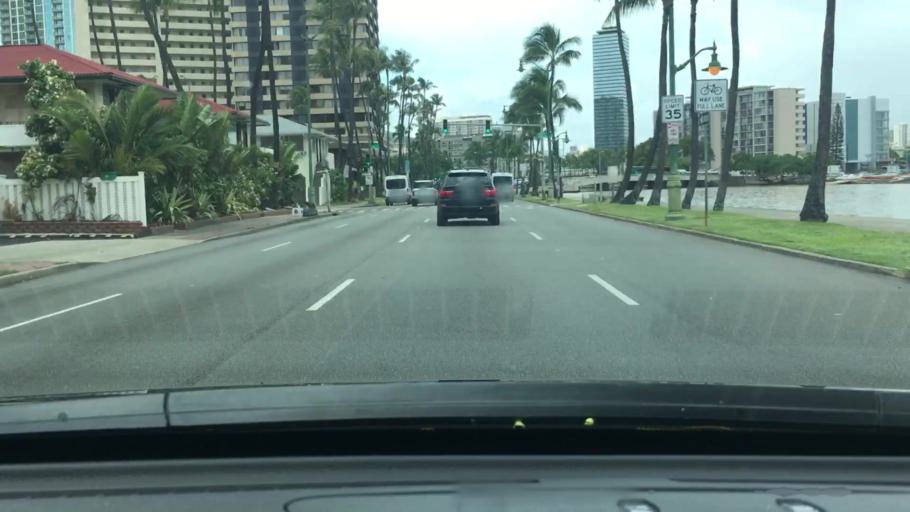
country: US
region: Hawaii
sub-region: Honolulu County
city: Honolulu
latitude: 21.2863
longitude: -157.8312
